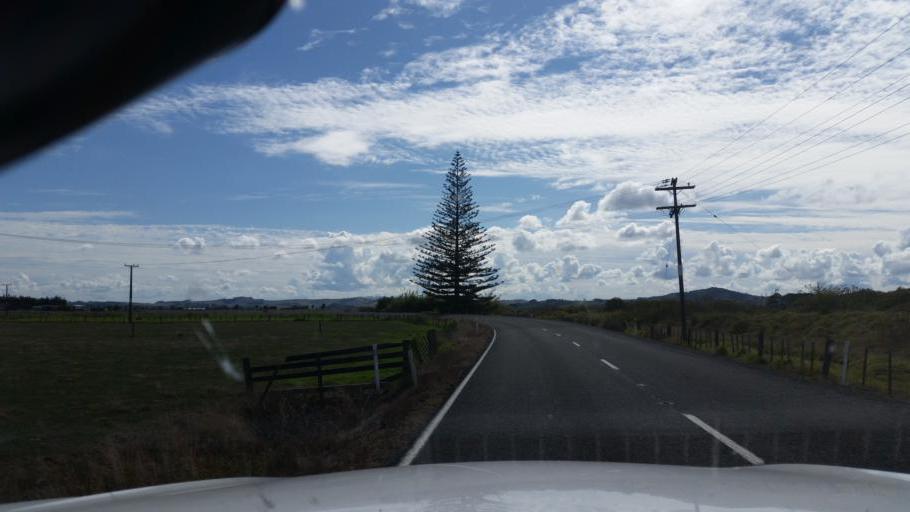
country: NZ
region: Northland
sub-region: Kaipara District
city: Dargaville
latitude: -36.1477
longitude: 174.0667
